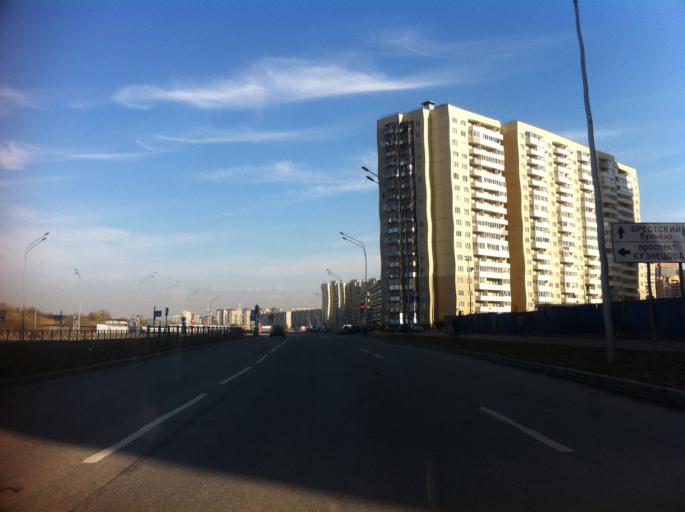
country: RU
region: St.-Petersburg
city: Uritsk
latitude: 59.8635
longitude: 30.1904
